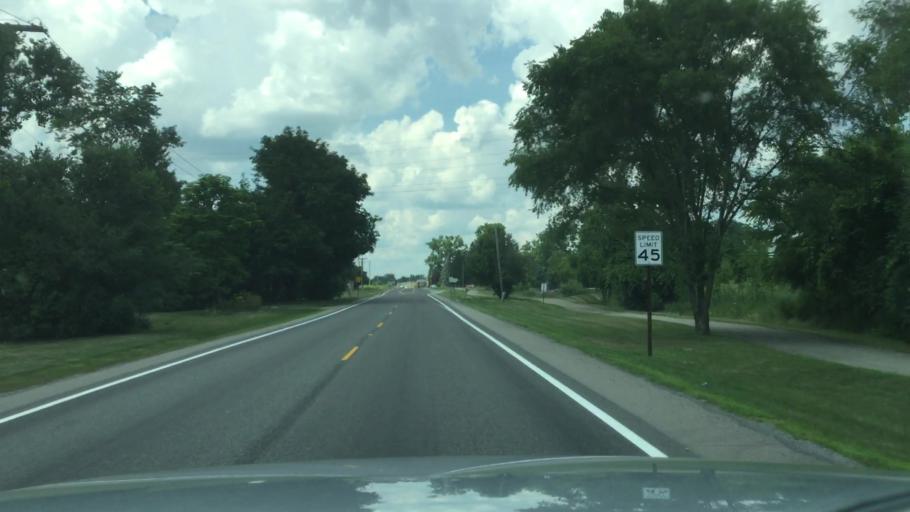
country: US
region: Michigan
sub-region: Washtenaw County
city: Ypsilanti
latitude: 42.2063
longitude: -83.6138
